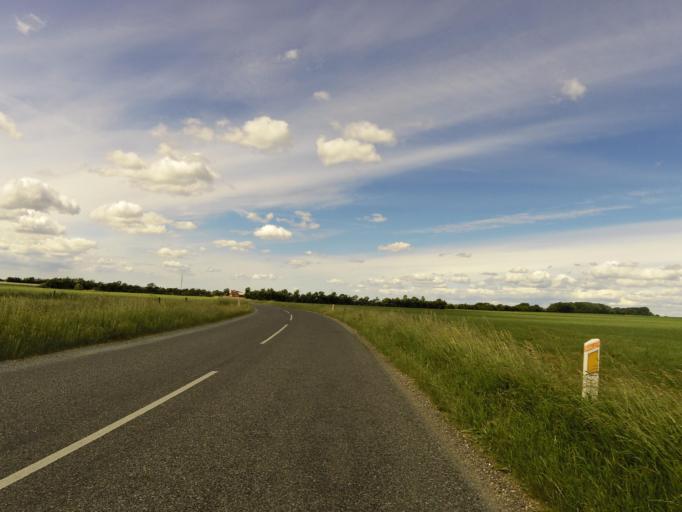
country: DK
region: South Denmark
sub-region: Esbjerg Kommune
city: Ribe
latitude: 55.2631
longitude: 8.8185
